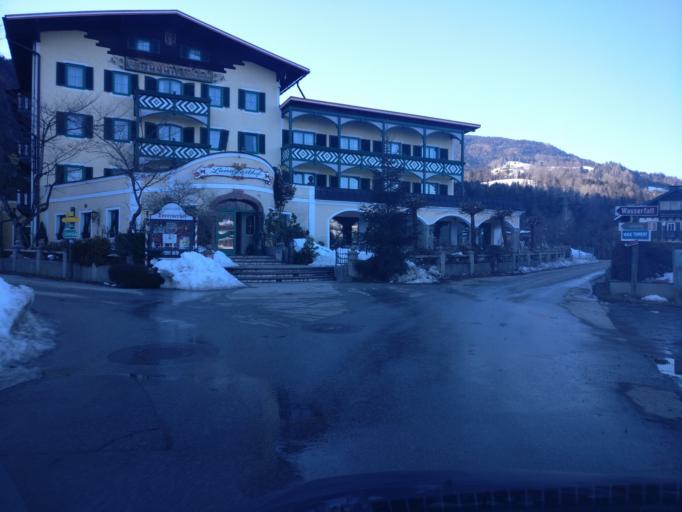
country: AT
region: Salzburg
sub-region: Politischer Bezirk Hallein
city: Golling an der Salzach
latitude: 47.6019
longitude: 13.1448
